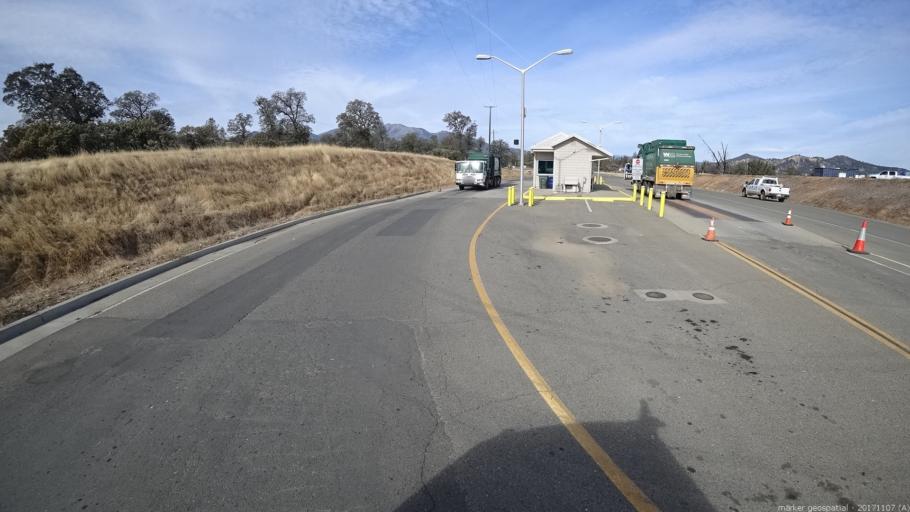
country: US
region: California
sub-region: Shasta County
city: Shasta
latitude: 40.4882
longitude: -122.5384
